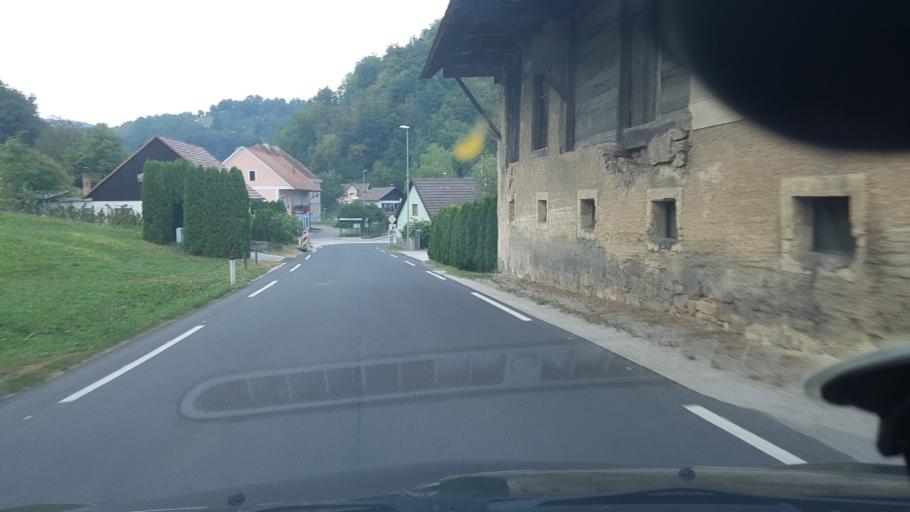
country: SI
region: Krsko
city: Senovo
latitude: 46.0380
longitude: 15.5194
